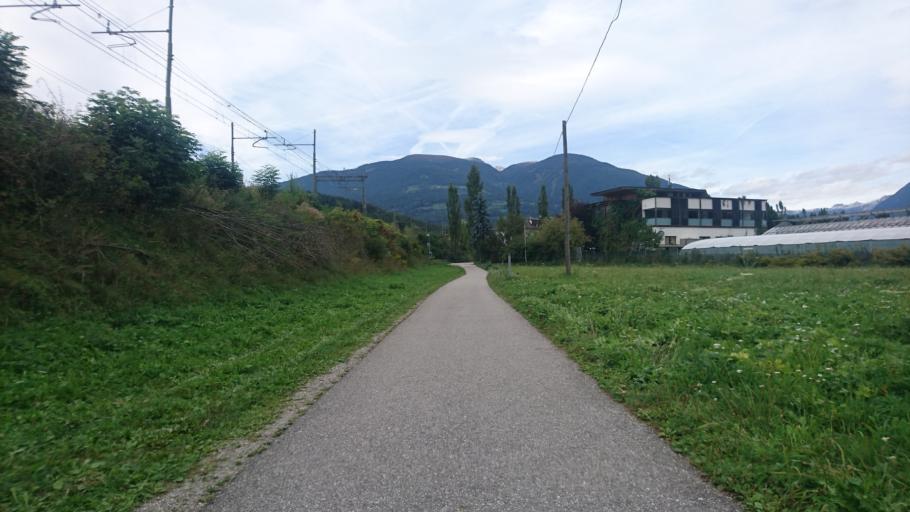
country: IT
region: Trentino-Alto Adige
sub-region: Bolzano
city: Brunico
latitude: 46.7881
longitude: 11.9254
